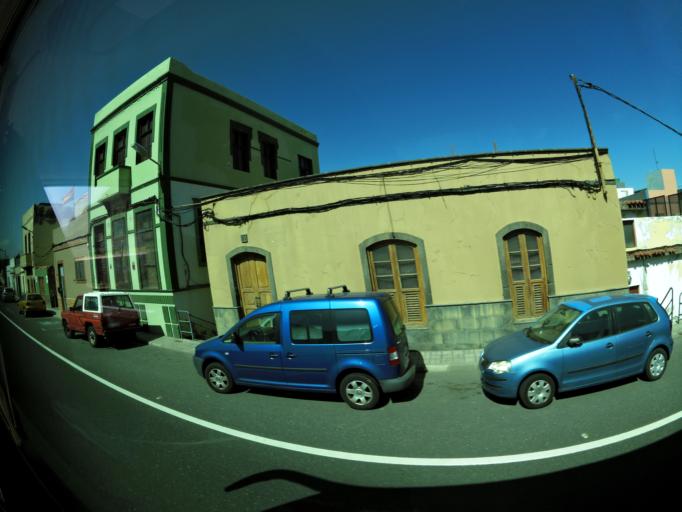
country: ES
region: Canary Islands
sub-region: Provincia de Las Palmas
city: Arucas
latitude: 28.1457
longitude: -15.5509
